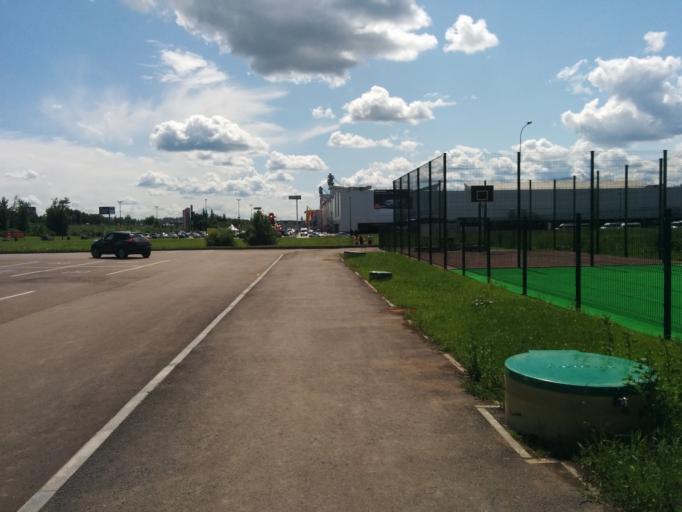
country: RU
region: Bashkortostan
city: Ufa
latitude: 54.6783
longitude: 55.9310
